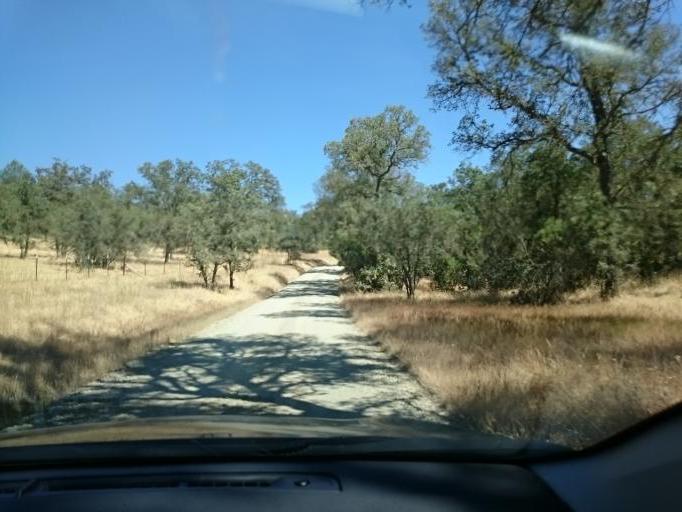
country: US
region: California
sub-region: Calaveras County
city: Rancho Calaveras
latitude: 38.0886
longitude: -120.7577
